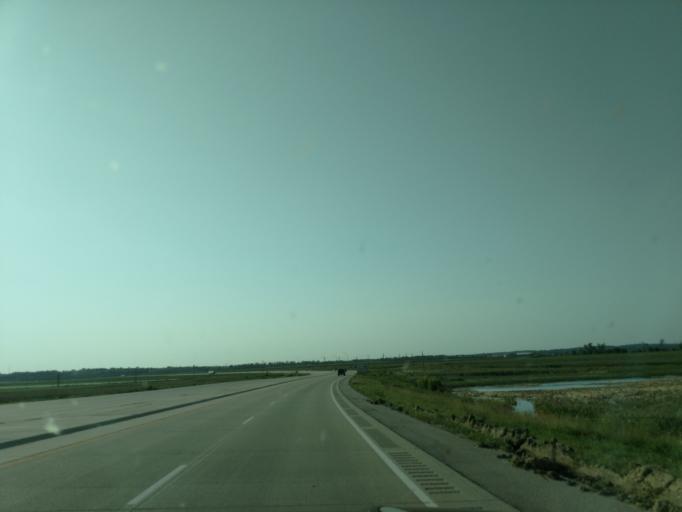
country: US
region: Nebraska
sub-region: Sarpy County
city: Offutt Air Force Base
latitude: 41.0725
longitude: -95.8862
